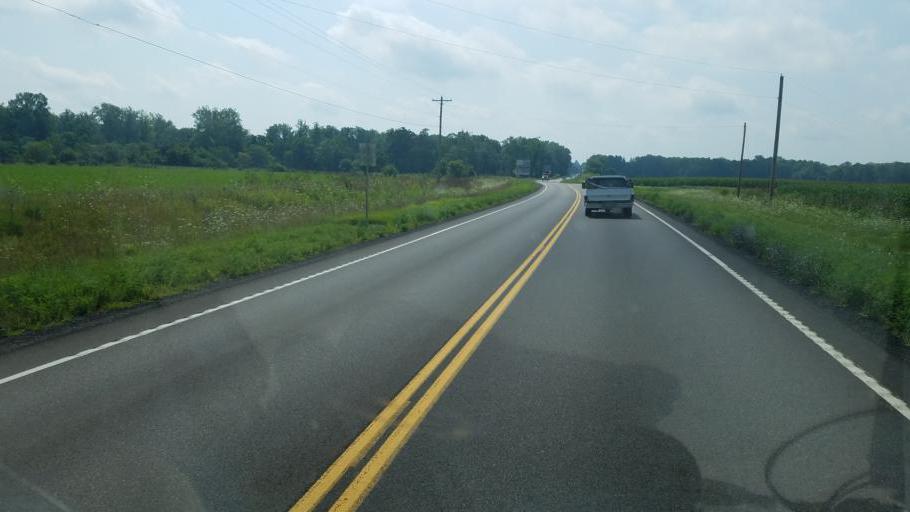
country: US
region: Ohio
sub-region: Knox County
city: Mount Vernon
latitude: 40.4269
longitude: -82.5092
